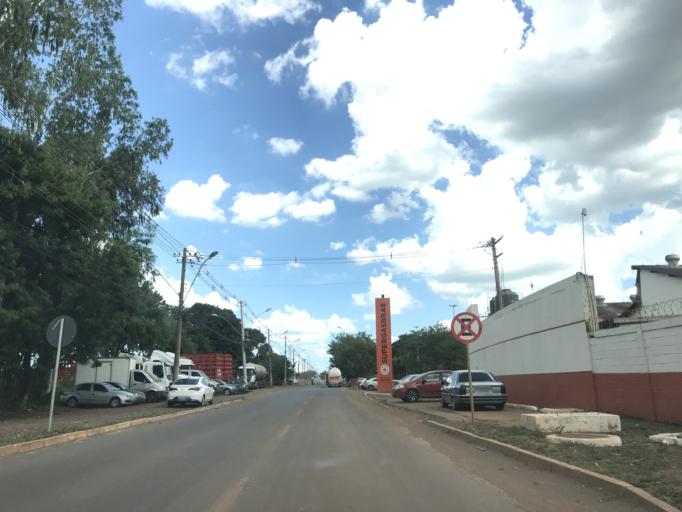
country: BR
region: Federal District
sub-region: Brasilia
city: Brasilia
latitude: -15.7963
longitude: -47.9766
